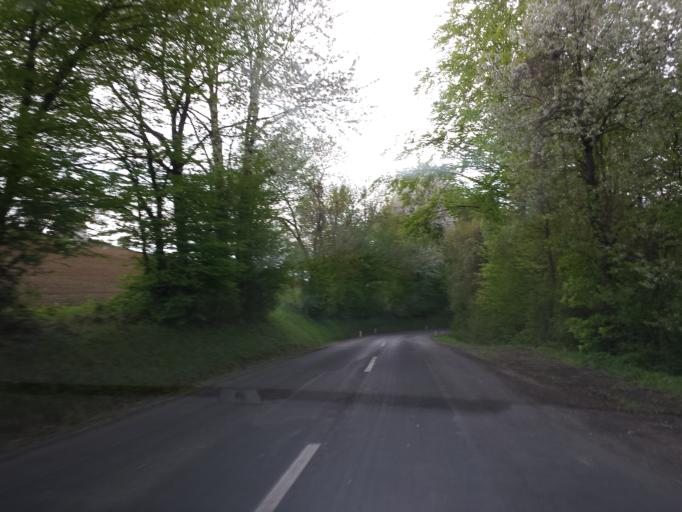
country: AT
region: Styria
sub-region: Politischer Bezirk Suedoststeiermark
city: Hatzendorf
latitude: 46.9911
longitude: 16.0140
